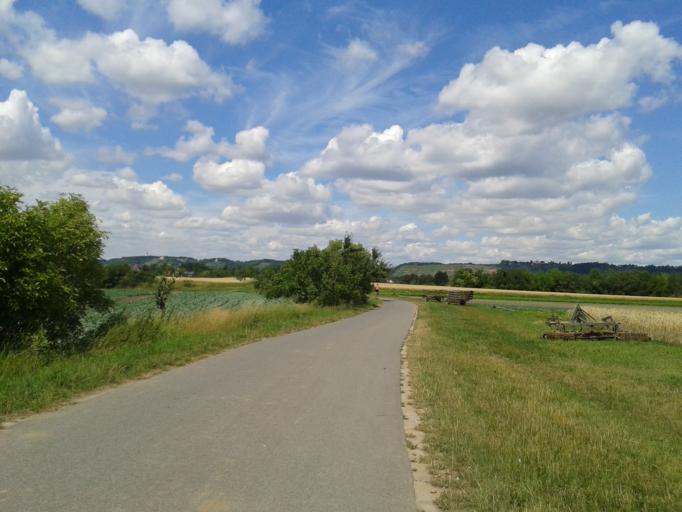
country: DE
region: Saxony
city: Radebeul
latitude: 51.0864
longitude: 13.6690
